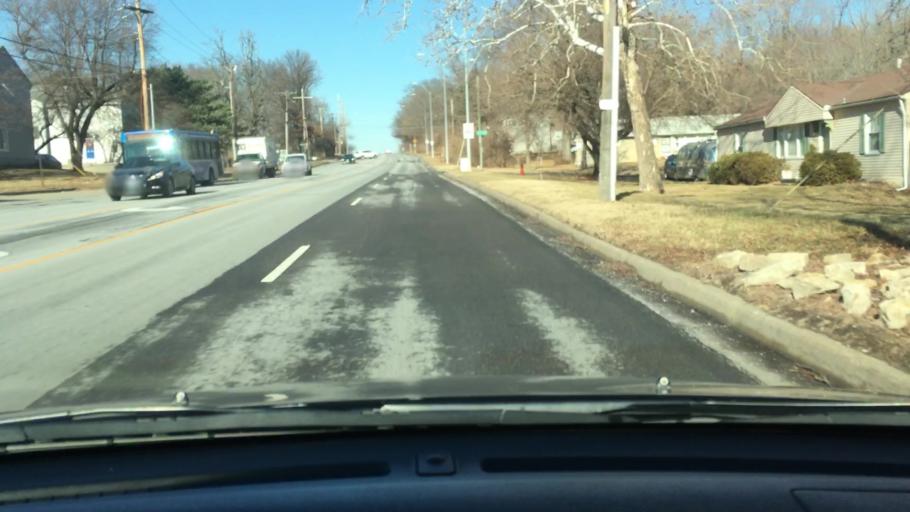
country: US
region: Kansas
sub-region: Johnson County
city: Leawood
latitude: 38.9511
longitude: -94.5960
